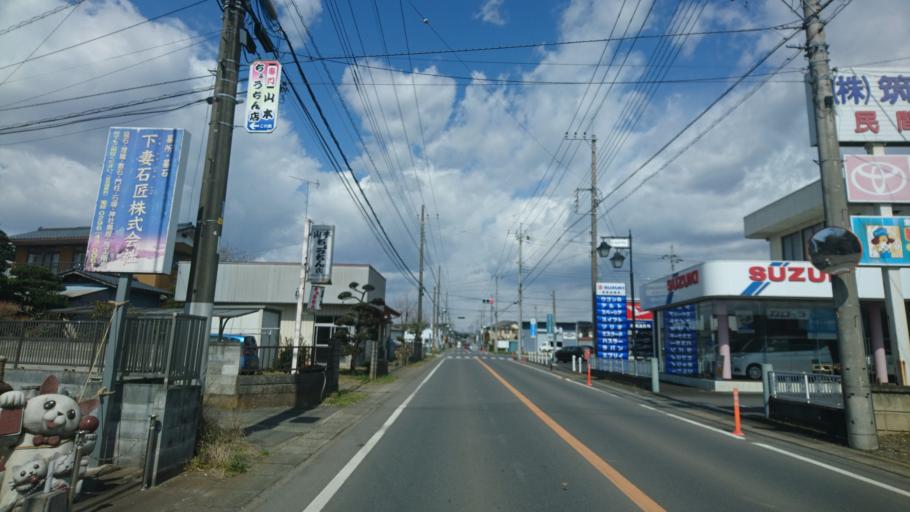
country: JP
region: Ibaraki
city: Ishige
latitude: 36.1967
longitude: 139.9524
